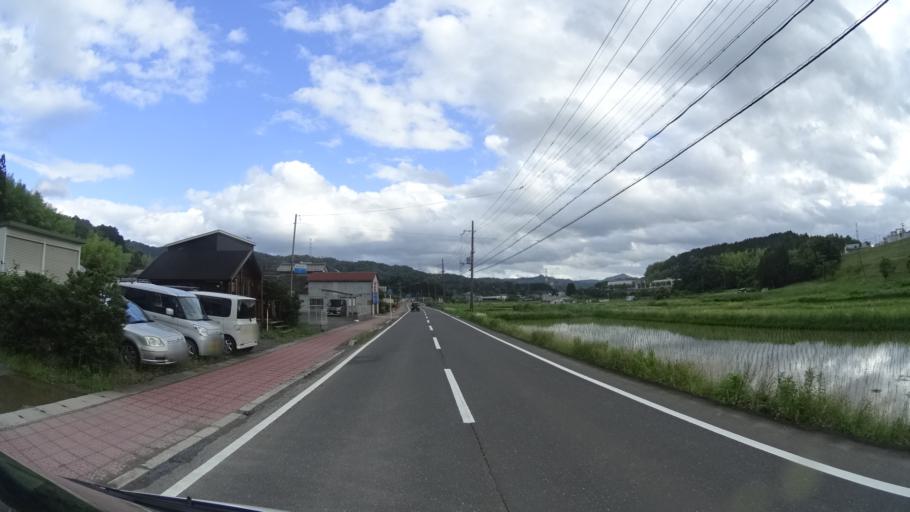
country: JP
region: Kyoto
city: Ayabe
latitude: 35.3319
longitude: 135.2926
